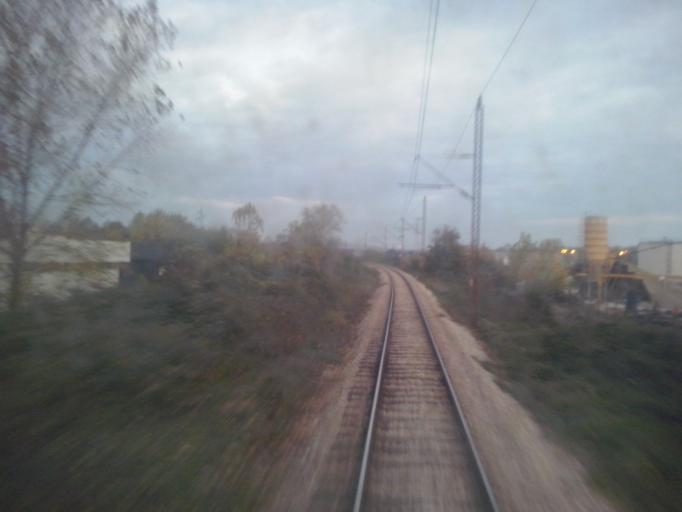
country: RS
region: Central Serbia
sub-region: Kolubarski Okrug
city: Valjevo
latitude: 44.2724
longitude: 19.9185
